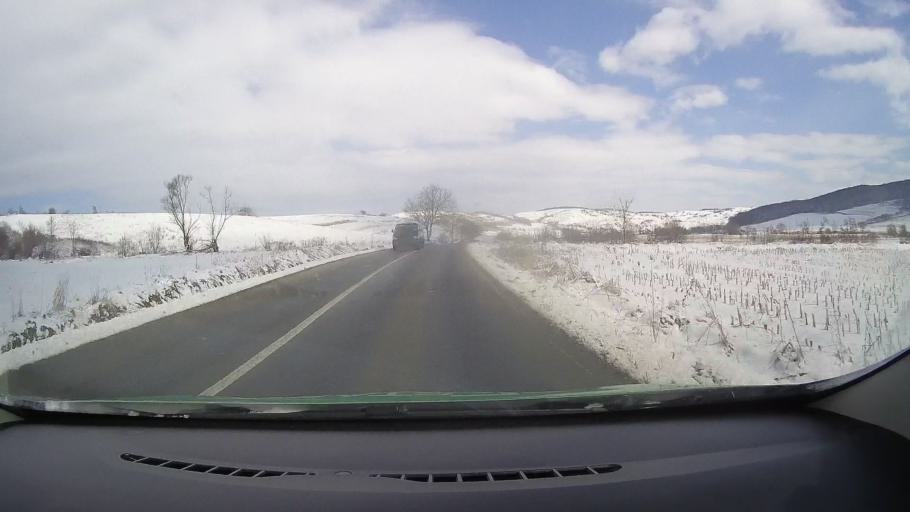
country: RO
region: Sibiu
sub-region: Comuna Altina
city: Altina
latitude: 45.9619
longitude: 24.4601
